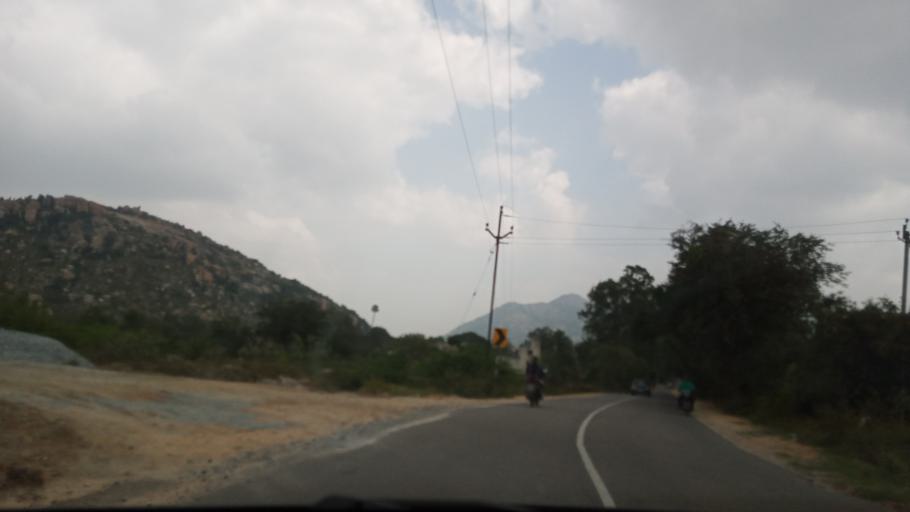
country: IN
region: Andhra Pradesh
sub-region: Chittoor
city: Madanapalle
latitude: 13.6417
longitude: 78.5718
